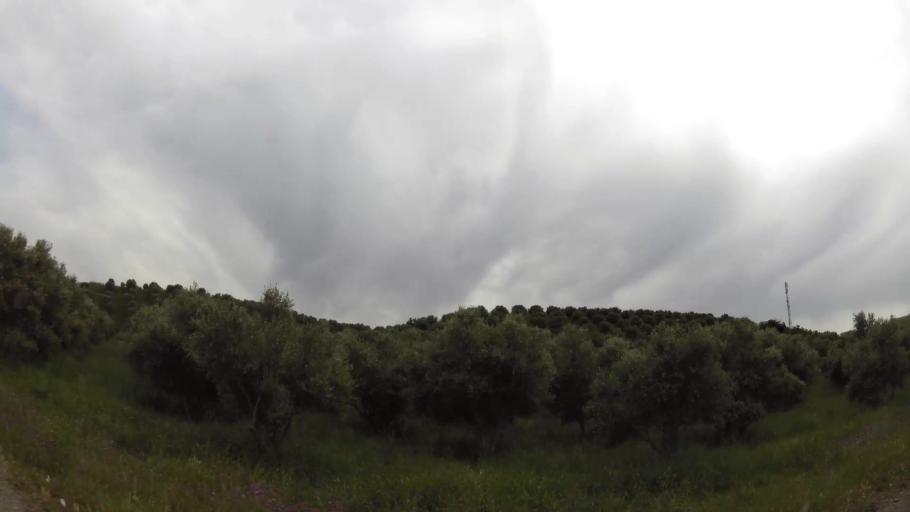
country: MA
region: Rabat-Sale-Zemmour-Zaer
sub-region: Khemisset
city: Khemisset
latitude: 33.7572
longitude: -6.2031
